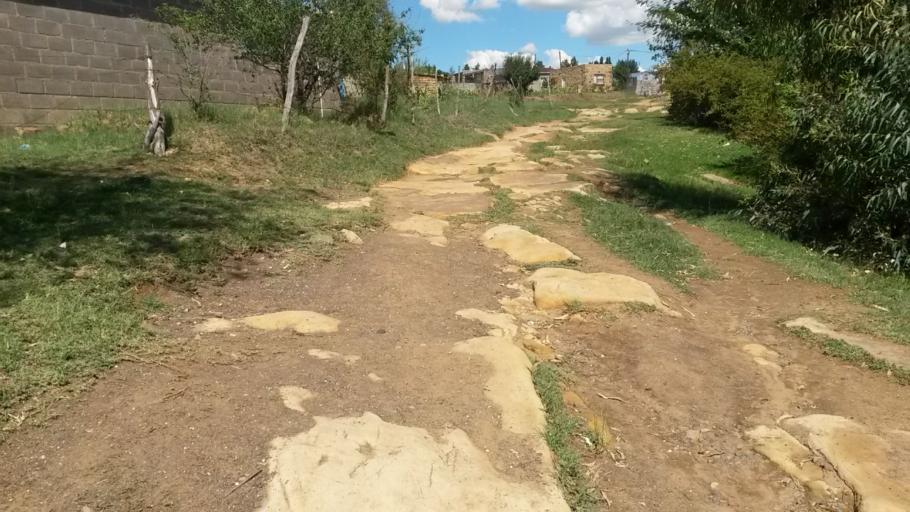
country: LS
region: Maseru
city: Maseru
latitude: -29.3683
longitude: 27.5033
